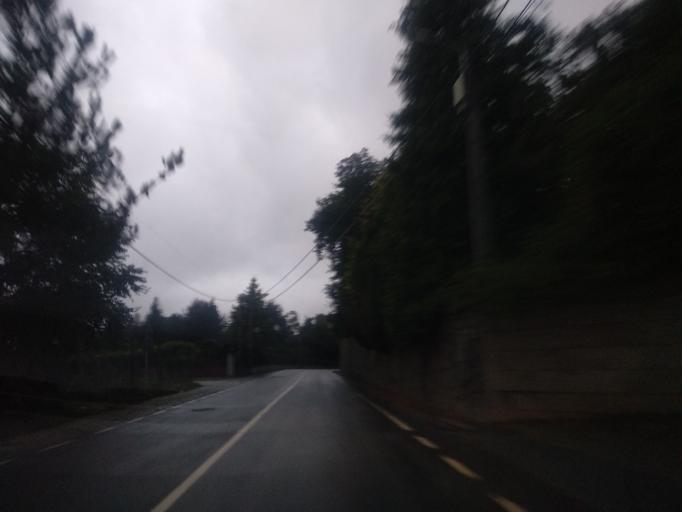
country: PT
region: Braga
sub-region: Guimaraes
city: Ponte
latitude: 41.4829
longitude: -8.3225
